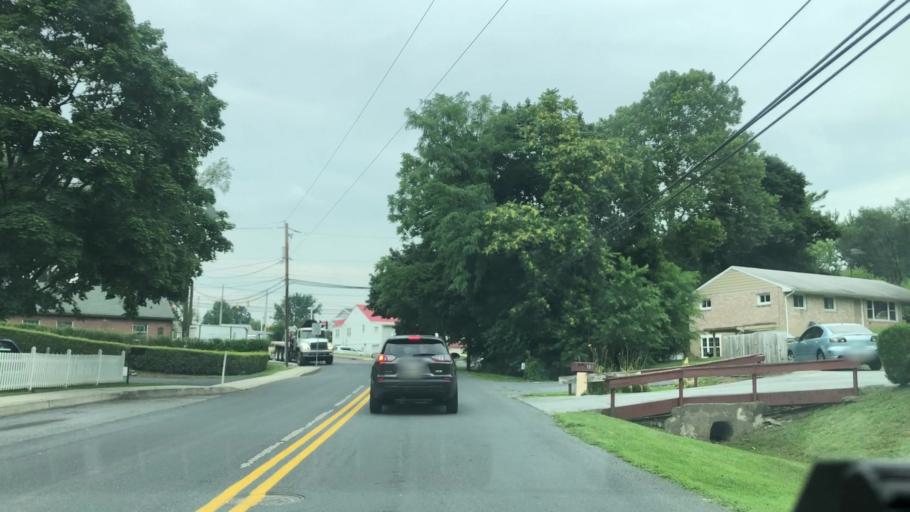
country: US
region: Pennsylvania
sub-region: Dauphin County
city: Colonial Park
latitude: 40.2913
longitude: -76.8092
